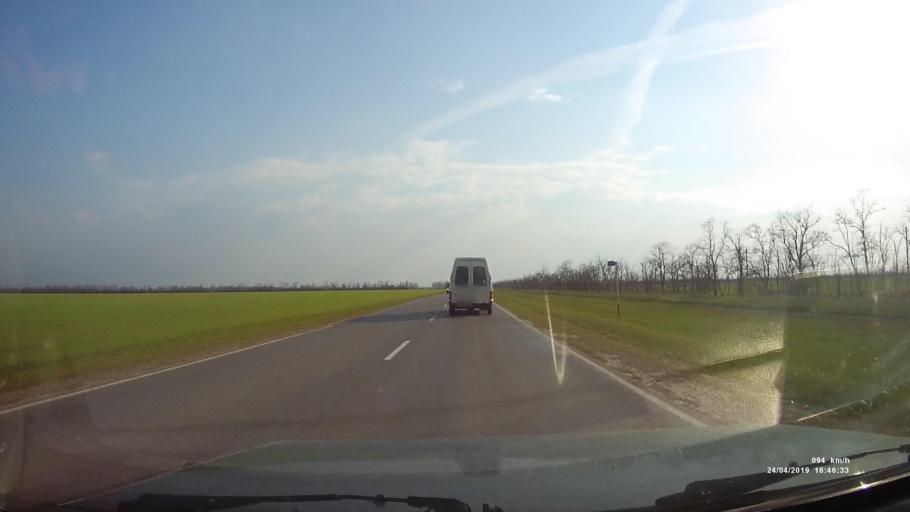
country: RU
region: Rostov
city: Proletarsk
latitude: 46.7559
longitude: 41.8001
